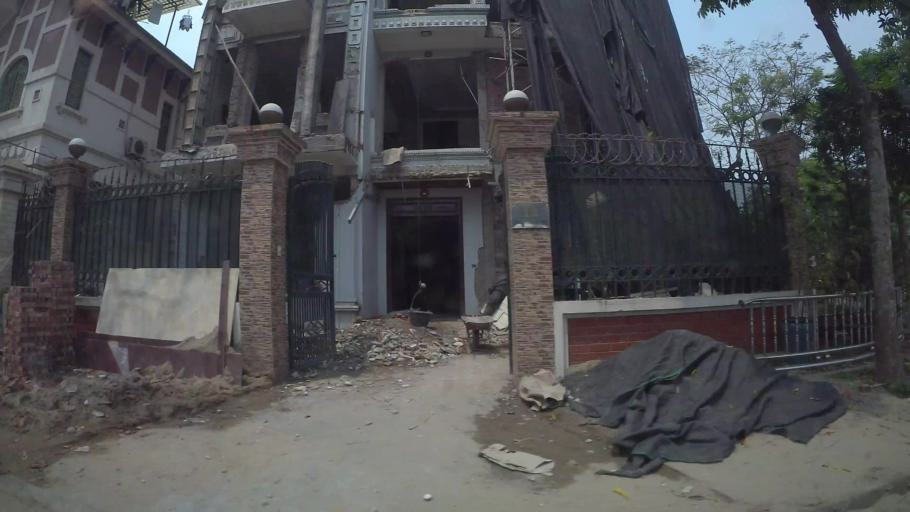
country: VN
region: Ha Noi
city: Van Dien
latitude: 20.9641
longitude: 105.8345
